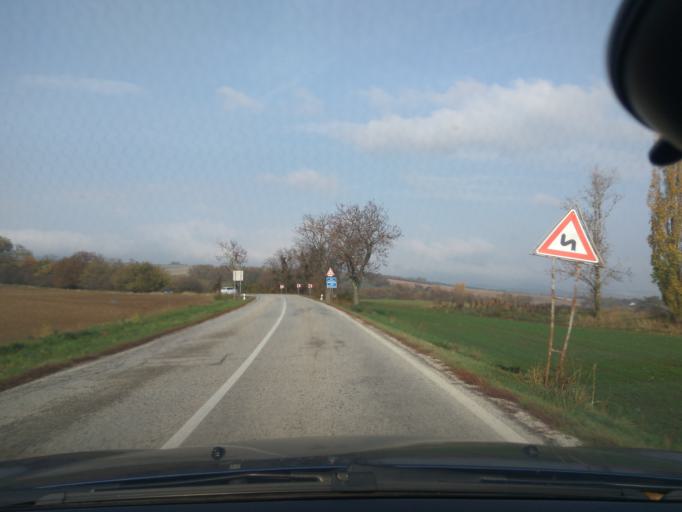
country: SK
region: Trnavsky
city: Vrbove
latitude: 48.6487
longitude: 17.7538
